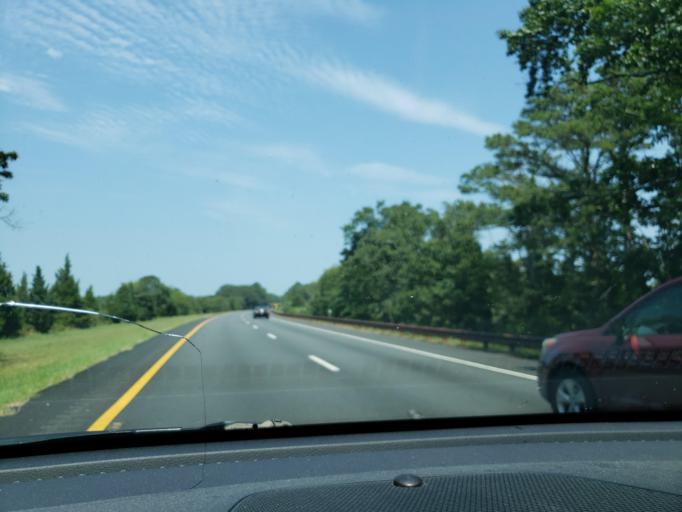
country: US
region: New Jersey
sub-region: Atlantic County
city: Somers Point
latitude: 39.3183
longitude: -74.6203
